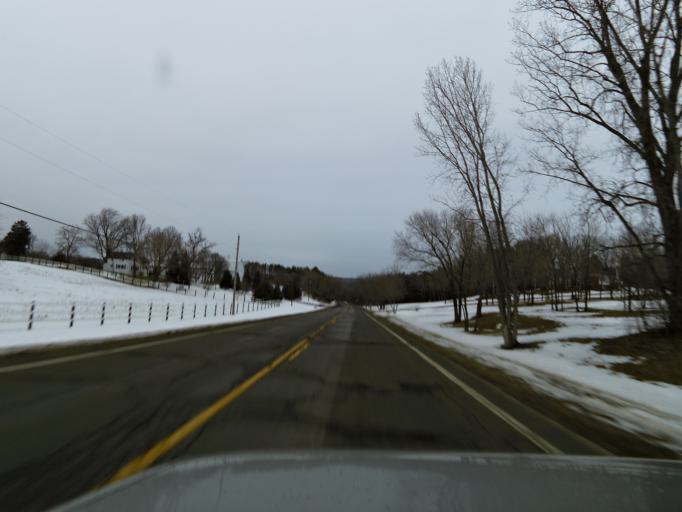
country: US
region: Minnesota
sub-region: Washington County
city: Afton
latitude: 44.8561
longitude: -92.7983
